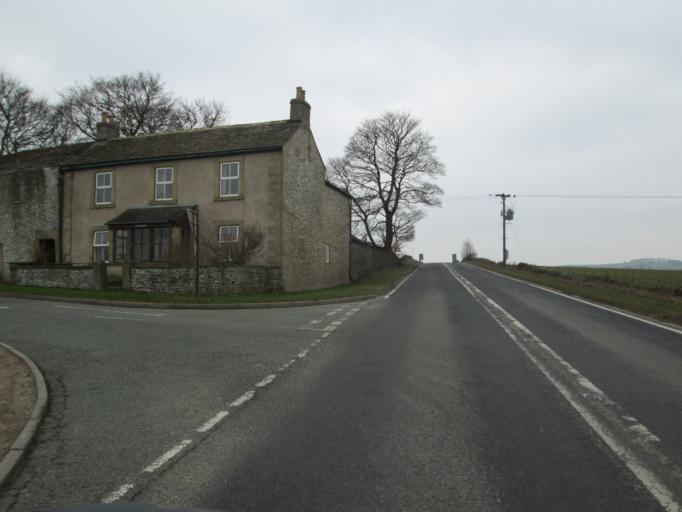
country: GB
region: England
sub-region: Derbyshire
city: Tideswell
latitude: 53.2783
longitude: -1.7375
